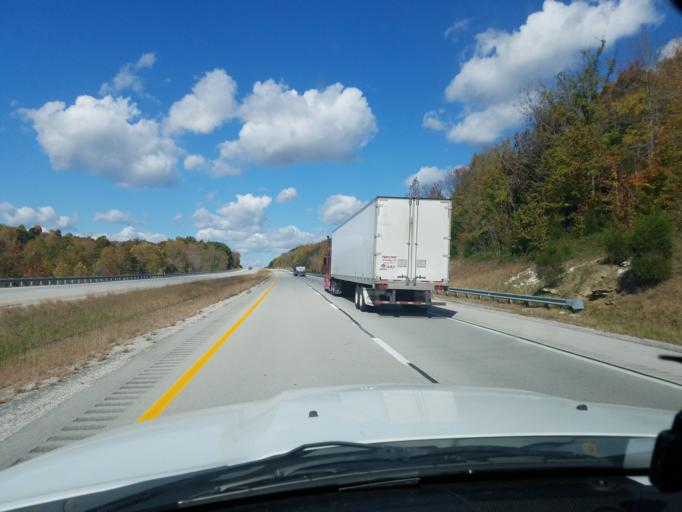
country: US
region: Kentucky
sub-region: Butler County
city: Morgantown
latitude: 37.2499
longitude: -86.7383
